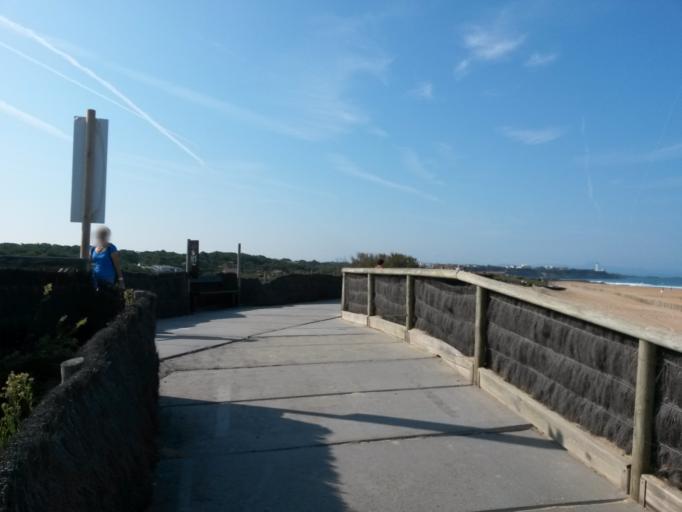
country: FR
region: Aquitaine
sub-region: Departement des Pyrenees-Atlantiques
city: Anglet
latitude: 43.5136
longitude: -1.5314
